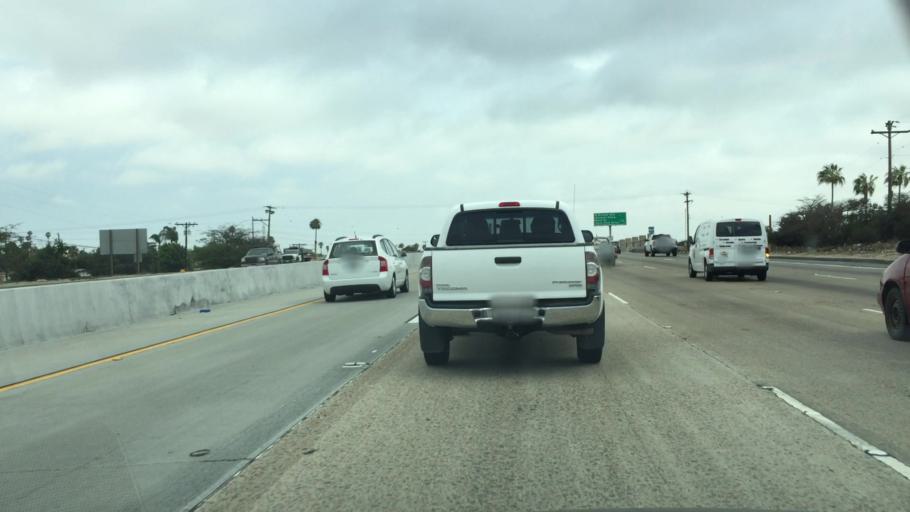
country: US
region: California
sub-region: San Diego County
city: Bonita
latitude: 32.6231
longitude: -117.0412
